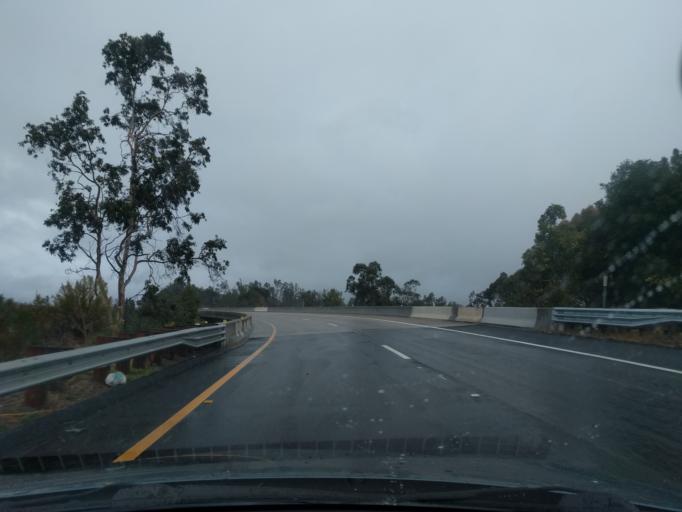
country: US
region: California
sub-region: San Diego County
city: La Mesa
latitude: 32.8214
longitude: -117.1152
